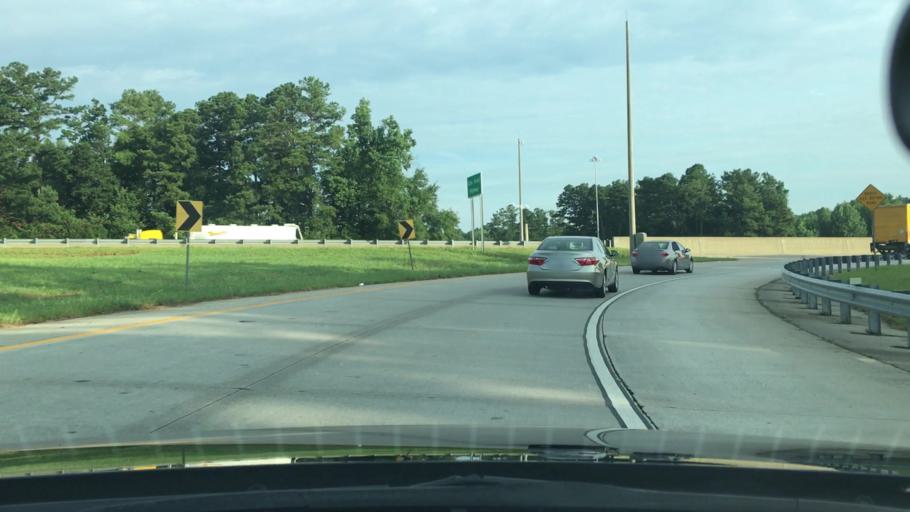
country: US
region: Georgia
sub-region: Coweta County
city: East Newnan
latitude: 33.3955
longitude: -84.7491
